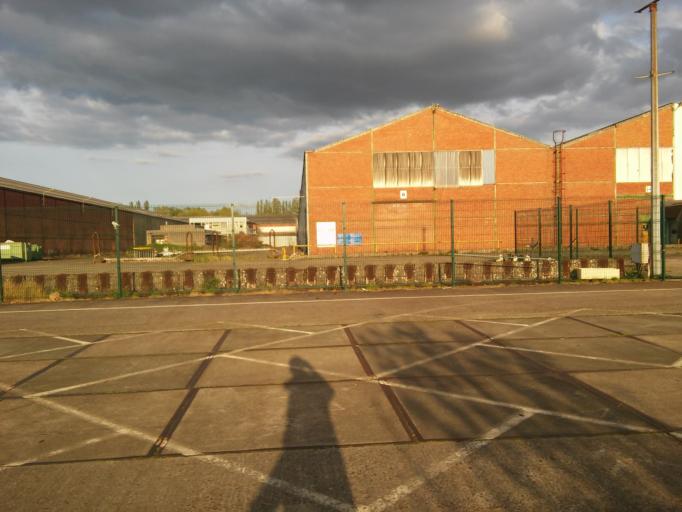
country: BE
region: Flanders
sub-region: Provincie Antwerpen
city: Hemiksem
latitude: 51.1351
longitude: 4.3282
